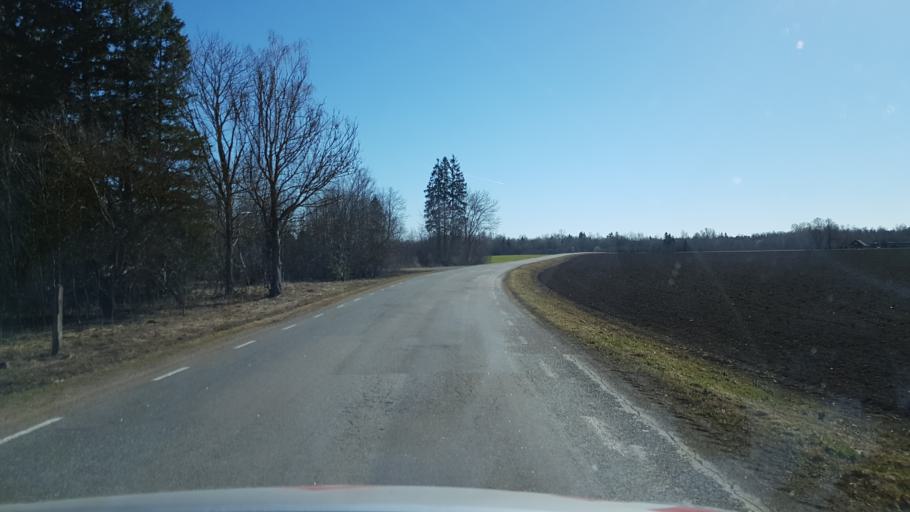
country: EE
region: Laeaene-Virumaa
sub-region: Someru vald
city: Someru
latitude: 59.3739
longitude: 26.4531
